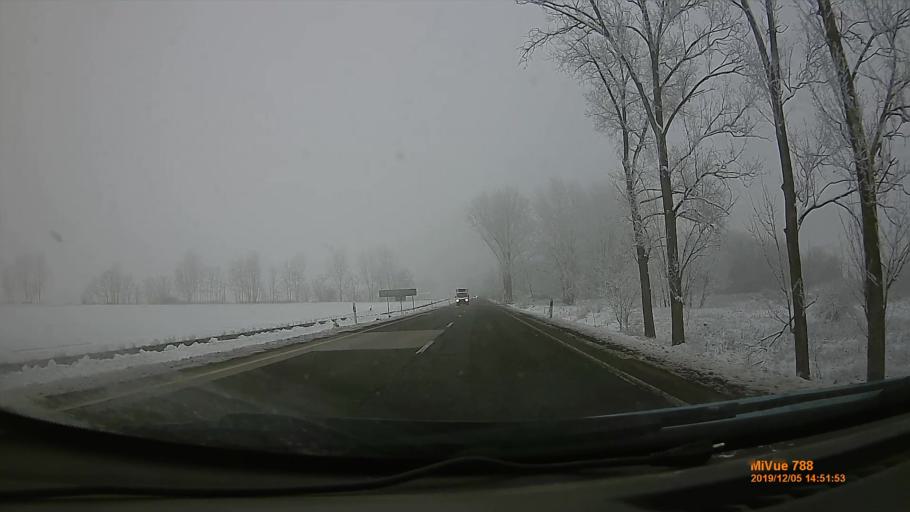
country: HU
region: Szabolcs-Szatmar-Bereg
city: Nyirtelek
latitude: 47.9964
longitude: 21.6514
